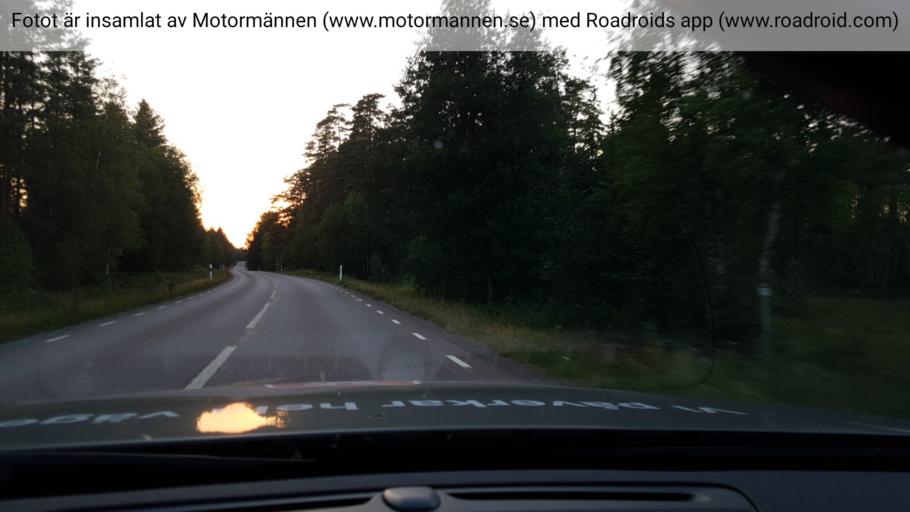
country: SE
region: Uppsala
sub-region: Heby Kommun
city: OEstervala
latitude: 60.0349
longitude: 17.2588
